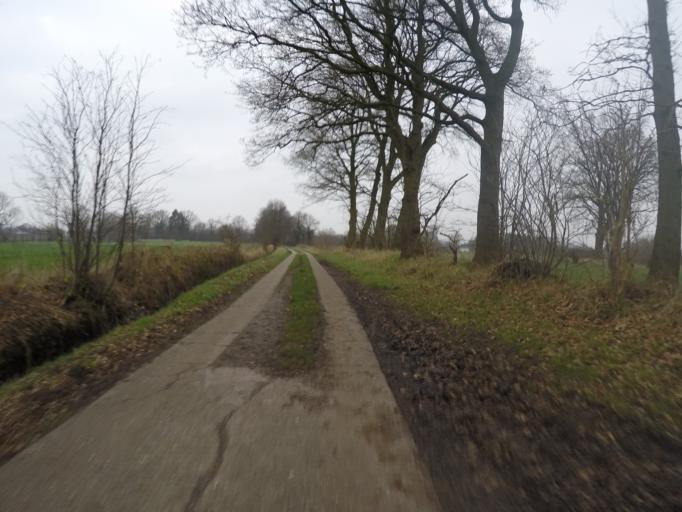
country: DE
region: Schleswig-Holstein
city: Borstel-Hohenraden
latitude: 53.6932
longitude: 9.8306
